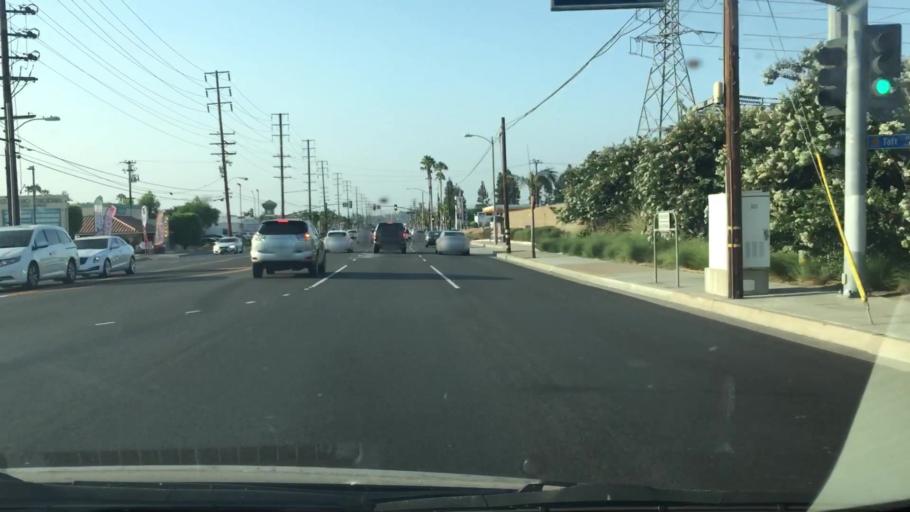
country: US
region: California
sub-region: Orange County
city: Villa Park
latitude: 33.8159
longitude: -117.8358
